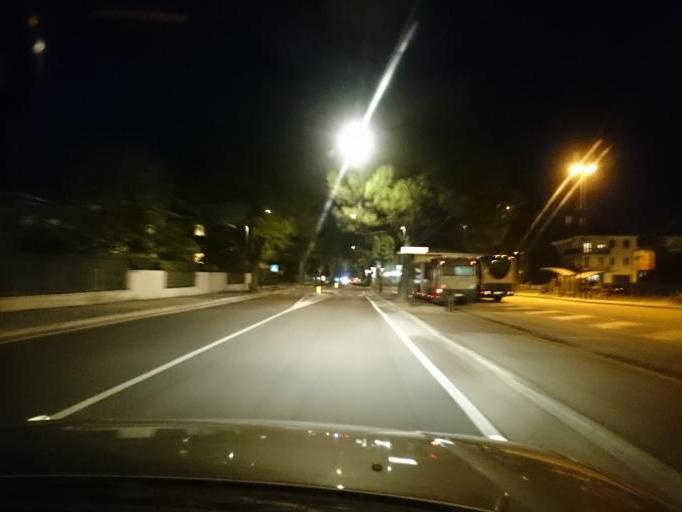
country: IT
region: Veneto
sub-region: Provincia di Padova
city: Este
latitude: 45.2288
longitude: 11.6619
